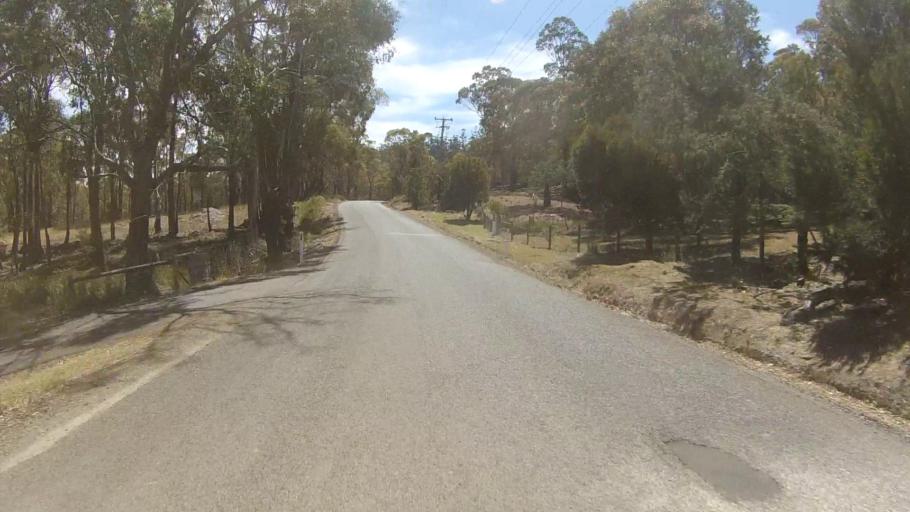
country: AU
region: Tasmania
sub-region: Kingborough
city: Blackmans Bay
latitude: -43.0272
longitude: 147.3129
